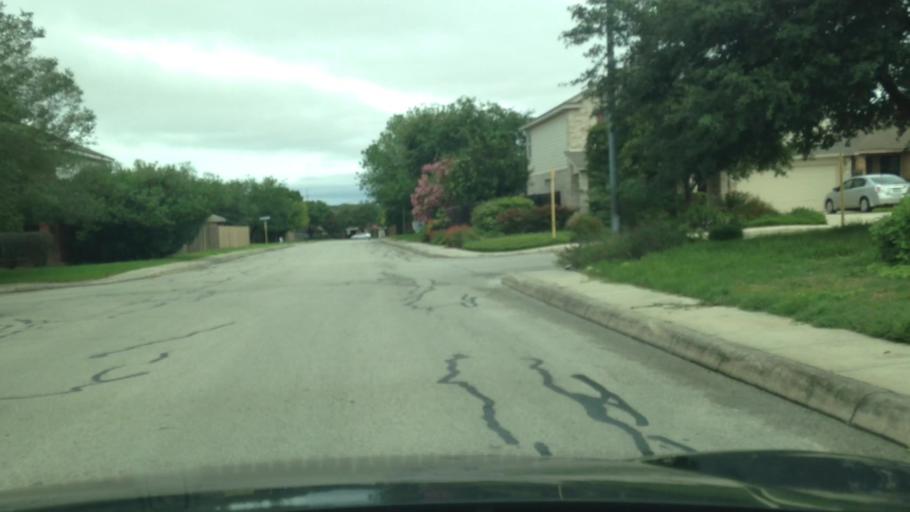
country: US
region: Texas
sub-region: Bexar County
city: Live Oak
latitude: 29.5843
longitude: -98.3872
